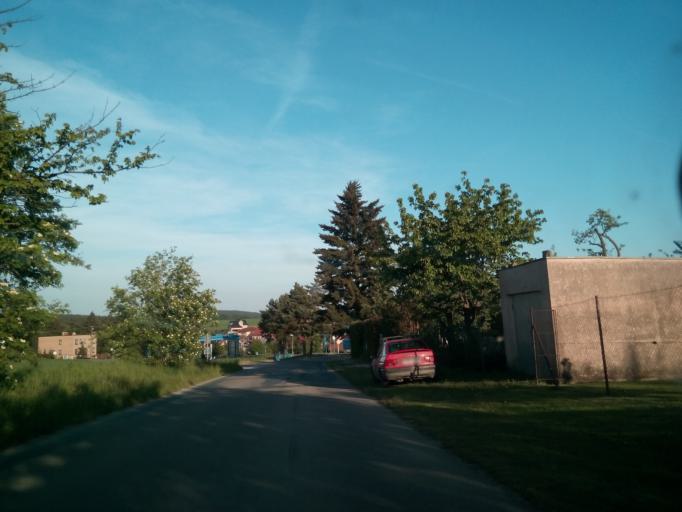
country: CZ
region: South Moravian
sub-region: Okres Blansko
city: Jedovnice
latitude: 49.3483
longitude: 16.7599
